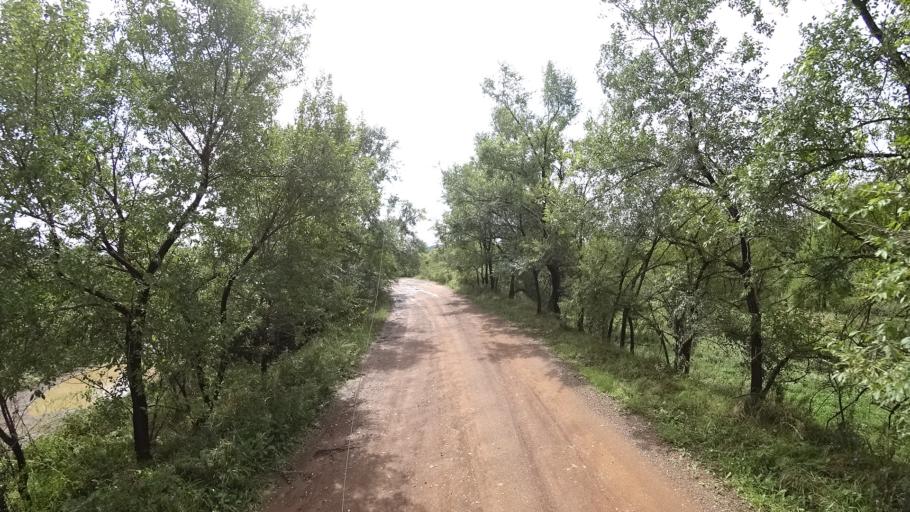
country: RU
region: Primorskiy
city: Monastyrishche
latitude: 44.1856
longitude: 132.4825
